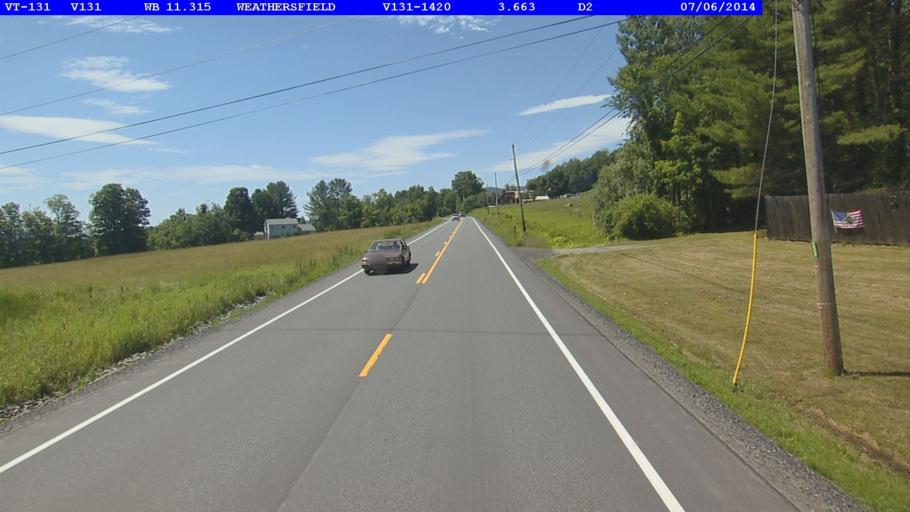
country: US
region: Vermont
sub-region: Windsor County
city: Windsor
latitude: 43.4238
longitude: -72.4909
